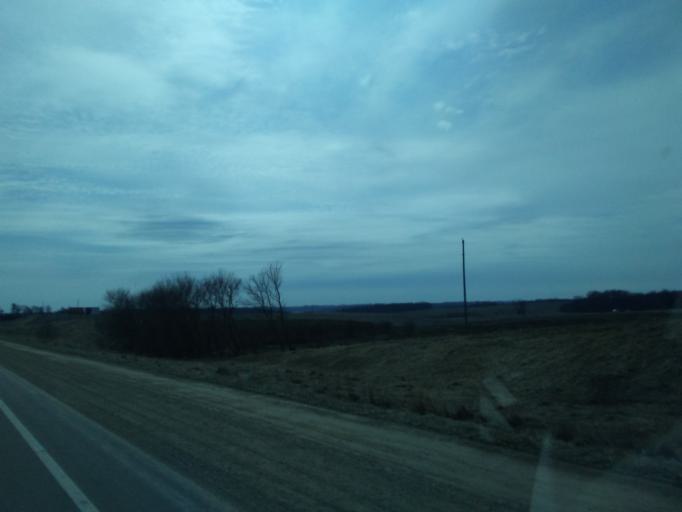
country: US
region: Iowa
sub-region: Winneshiek County
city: Decorah
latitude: 43.3616
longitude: -91.8043
